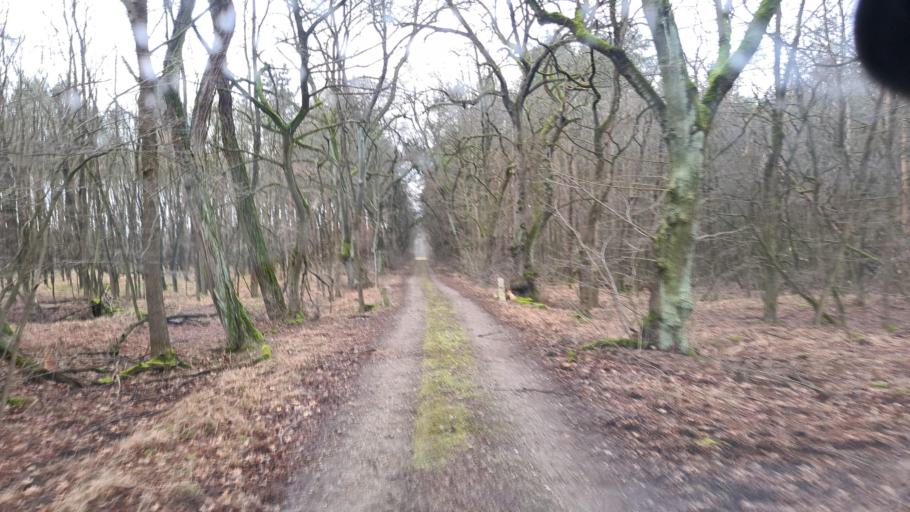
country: DE
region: Brandenburg
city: Kroppen
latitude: 51.3982
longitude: 13.7788
